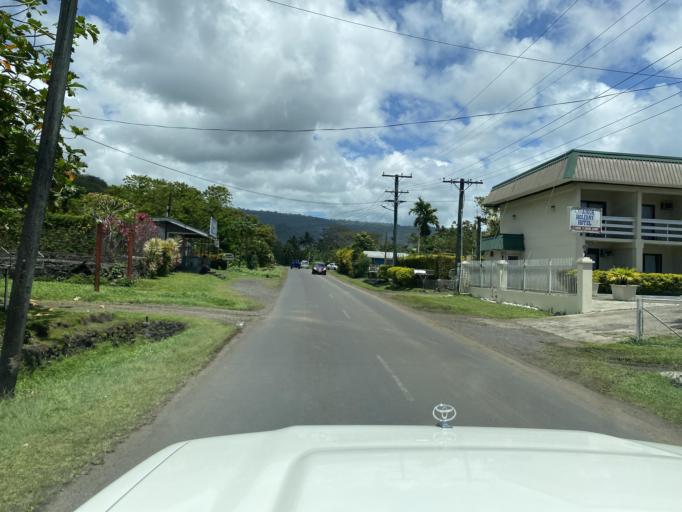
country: WS
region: Tuamasaga
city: Apia
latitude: -13.8481
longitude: -171.7785
